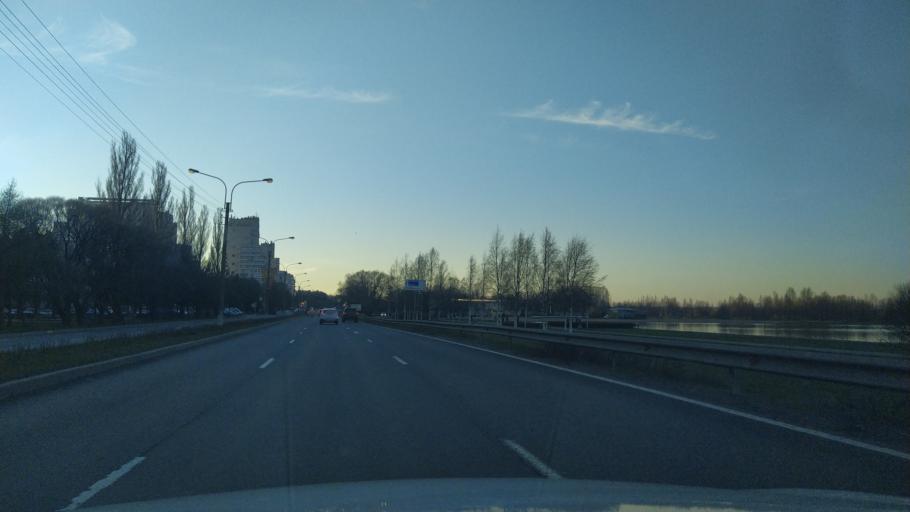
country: RU
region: St.-Petersburg
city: Sestroretsk
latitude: 60.1022
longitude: 29.9790
